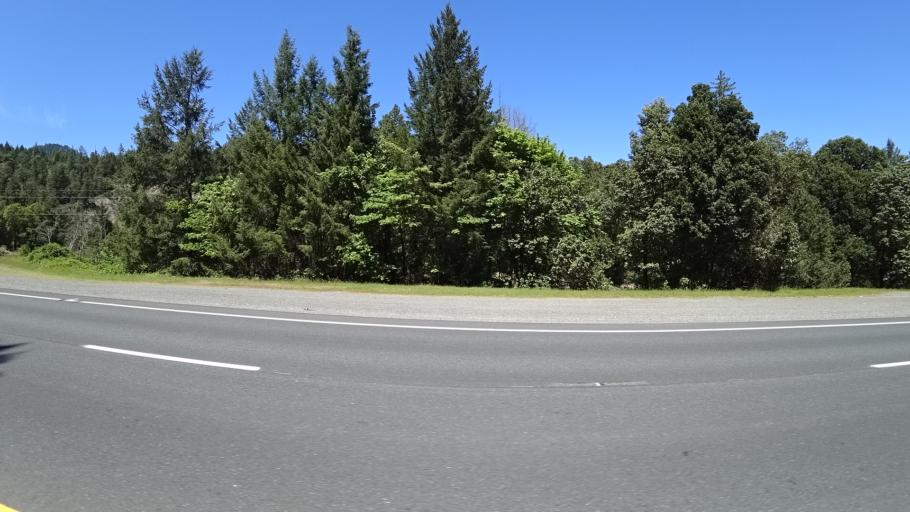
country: US
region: California
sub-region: Humboldt County
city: Willow Creek
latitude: 40.9441
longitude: -123.6623
